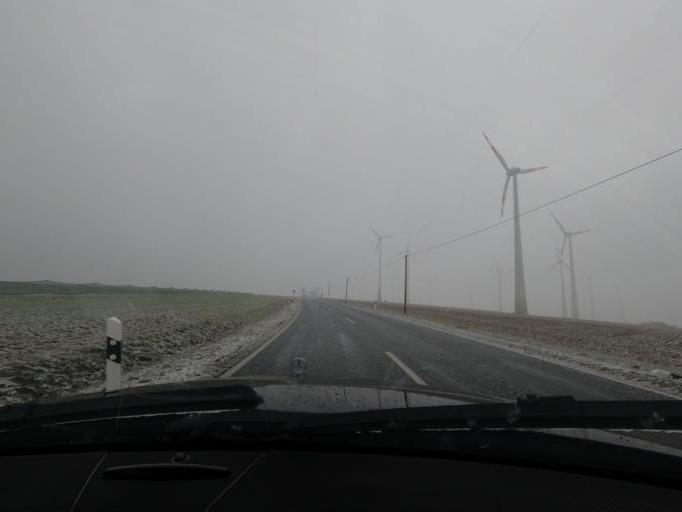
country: DE
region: Thuringia
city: Buttstedt
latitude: 51.2314
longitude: 10.2975
